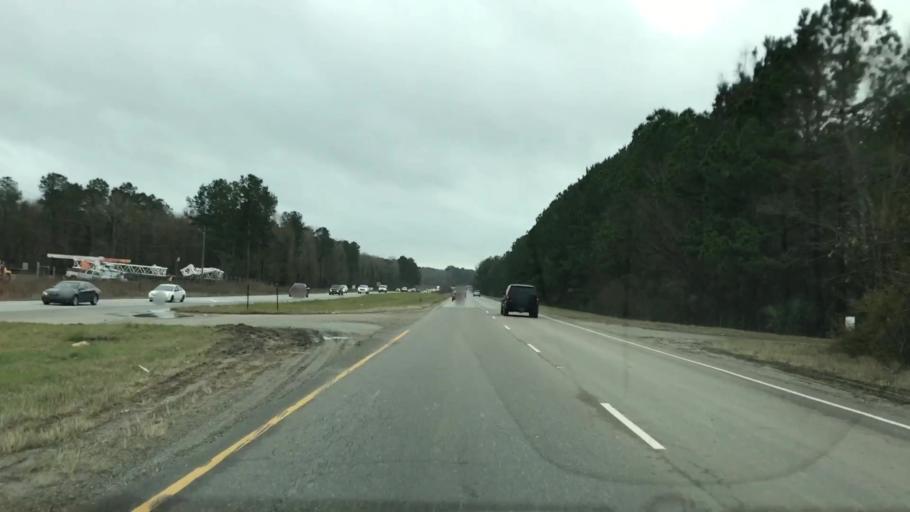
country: US
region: South Carolina
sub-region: Berkeley County
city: Goose Creek
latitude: 33.0551
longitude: -80.0348
